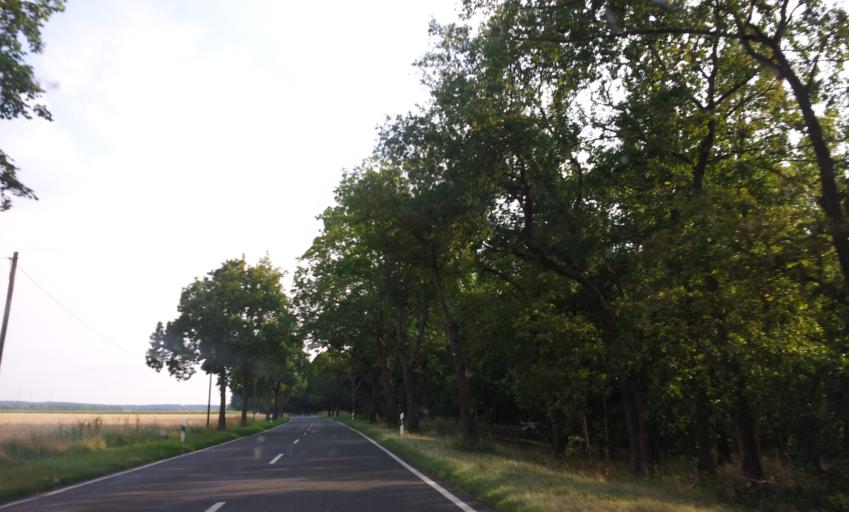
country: DE
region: Brandenburg
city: Treuenbrietzen
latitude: 52.0991
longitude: 12.9485
